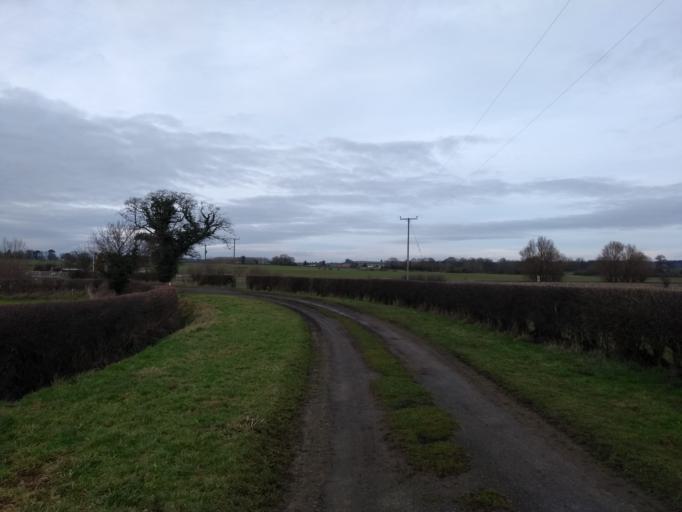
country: GB
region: England
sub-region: East Riding of Yorkshire
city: Stamford Bridge
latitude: 54.0682
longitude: -0.9335
